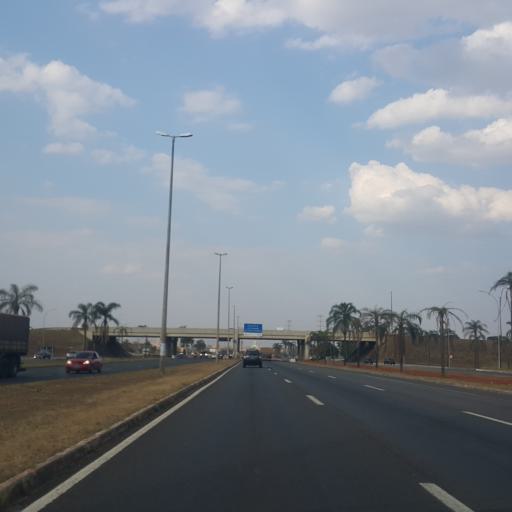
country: BR
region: Federal District
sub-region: Brasilia
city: Brasilia
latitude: -15.8831
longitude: -48.0623
